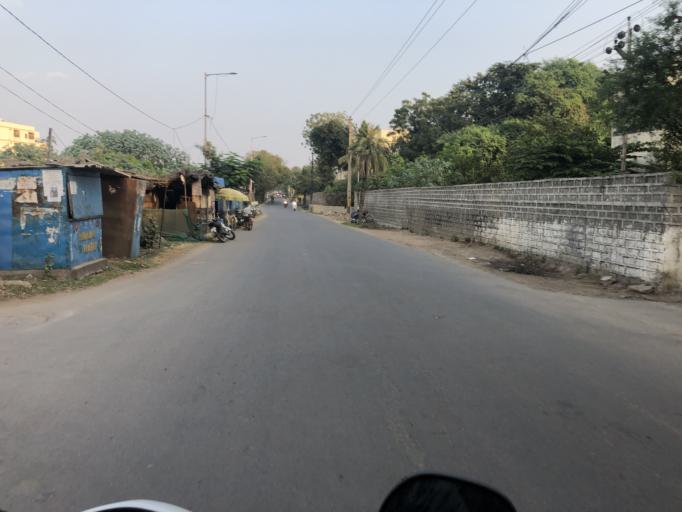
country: IN
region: Telangana
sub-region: Rangareddi
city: Kukatpalli
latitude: 17.4627
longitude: 78.4345
